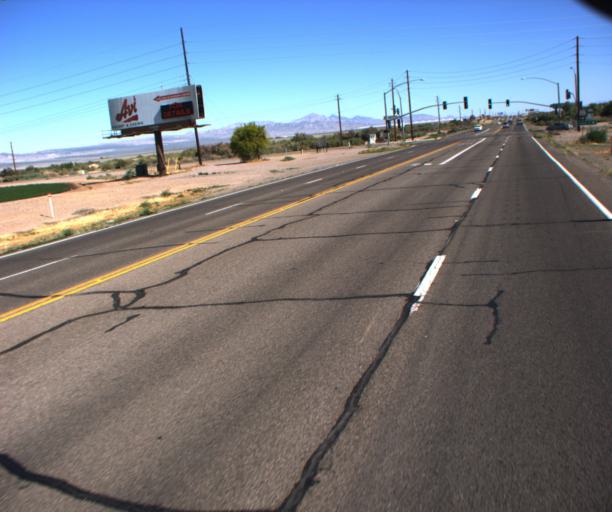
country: US
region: Arizona
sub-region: Mohave County
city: Mohave Valley
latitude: 34.9668
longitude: -114.5979
